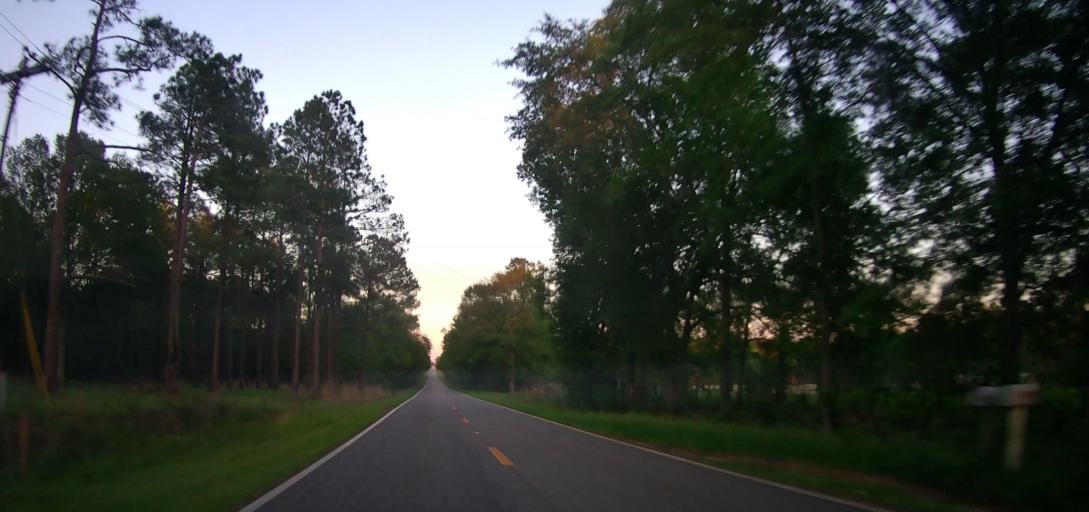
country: US
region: Georgia
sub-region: Wilcox County
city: Rochelle
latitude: 31.7831
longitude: -83.4273
